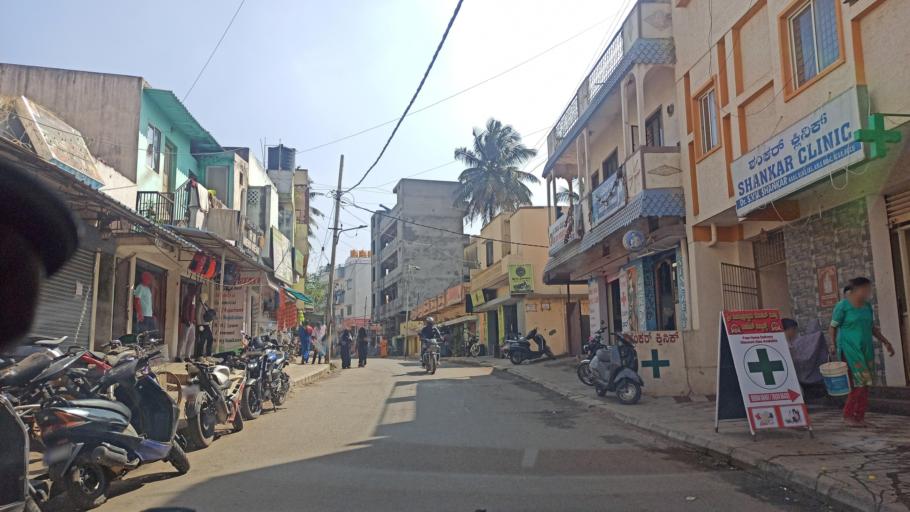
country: IN
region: Karnataka
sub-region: Bangalore Urban
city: Yelahanka
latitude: 13.0425
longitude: 77.5739
